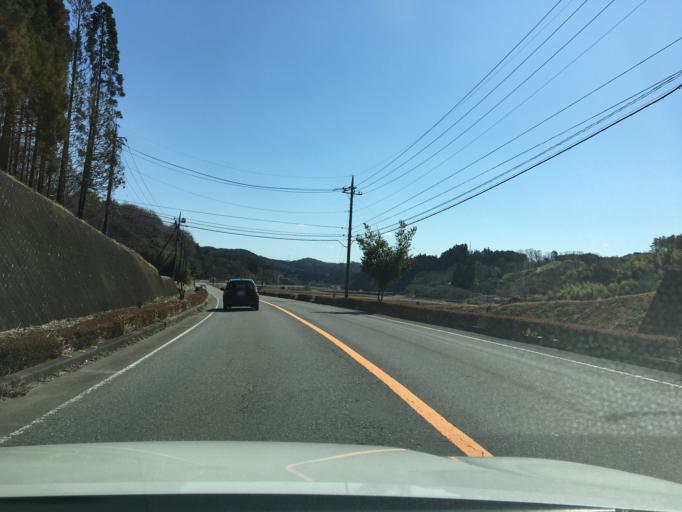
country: JP
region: Tochigi
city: Kuroiso
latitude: 37.0310
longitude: 140.1735
